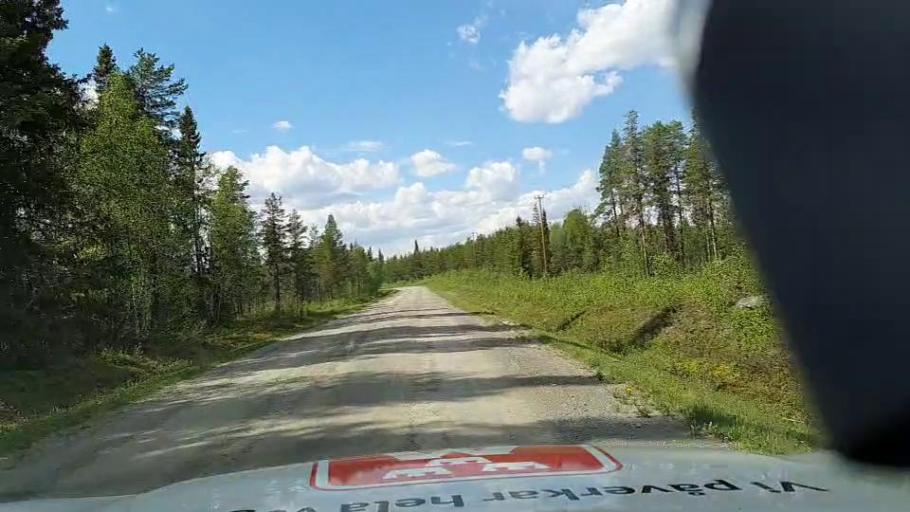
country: SE
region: Vaesterbotten
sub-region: Vilhelmina Kommun
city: Sjoberg
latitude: 64.5444
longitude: 15.6463
